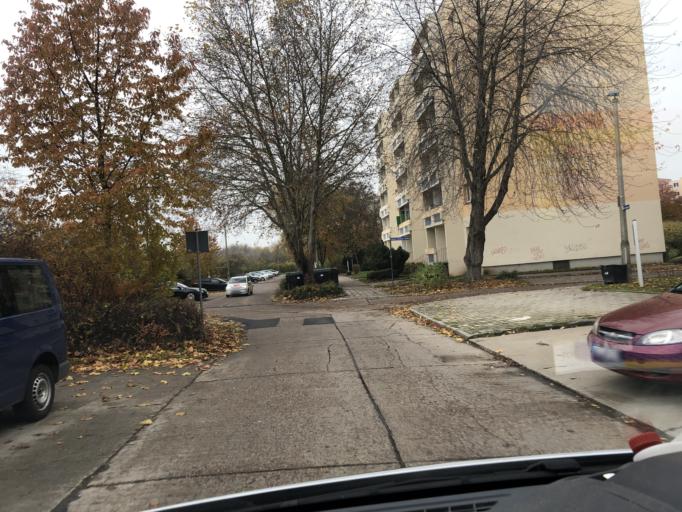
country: DE
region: Saxony-Anhalt
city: Halle Neustadt
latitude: 51.4664
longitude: 11.9242
